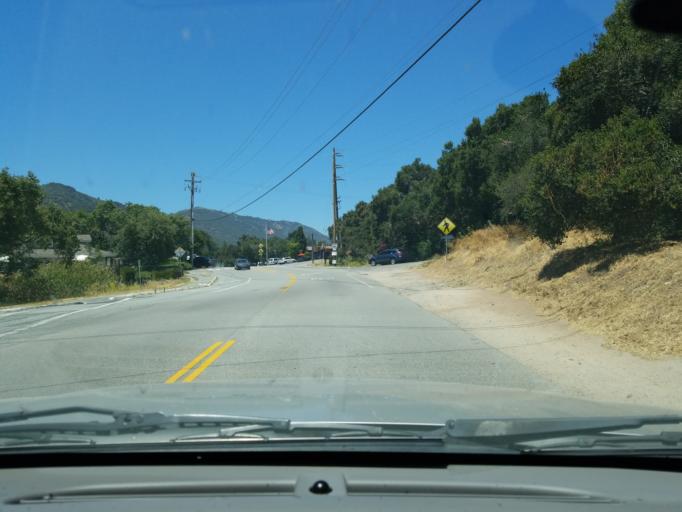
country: US
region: California
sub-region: Monterey County
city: Carmel Valley Village
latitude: 36.4777
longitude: -121.7276
